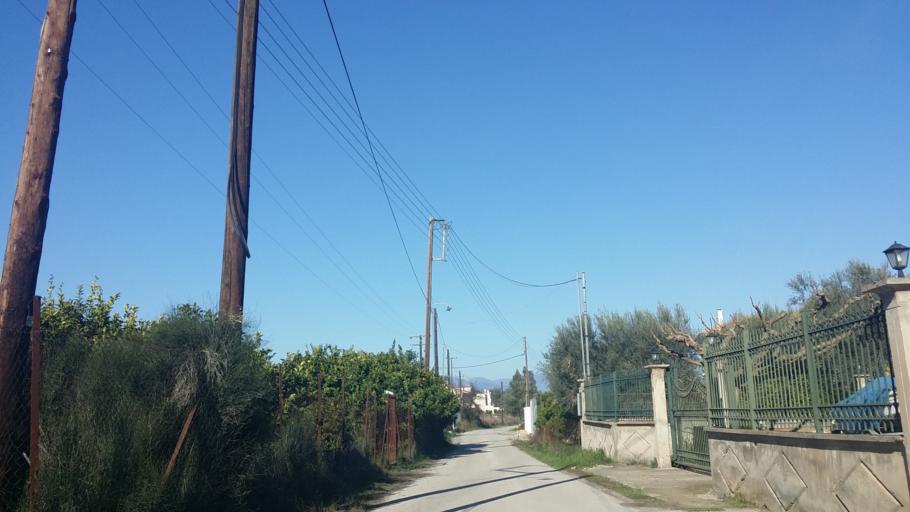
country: GR
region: West Greece
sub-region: Nomos Achaias
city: Temeni
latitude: 38.1975
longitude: 22.1797
